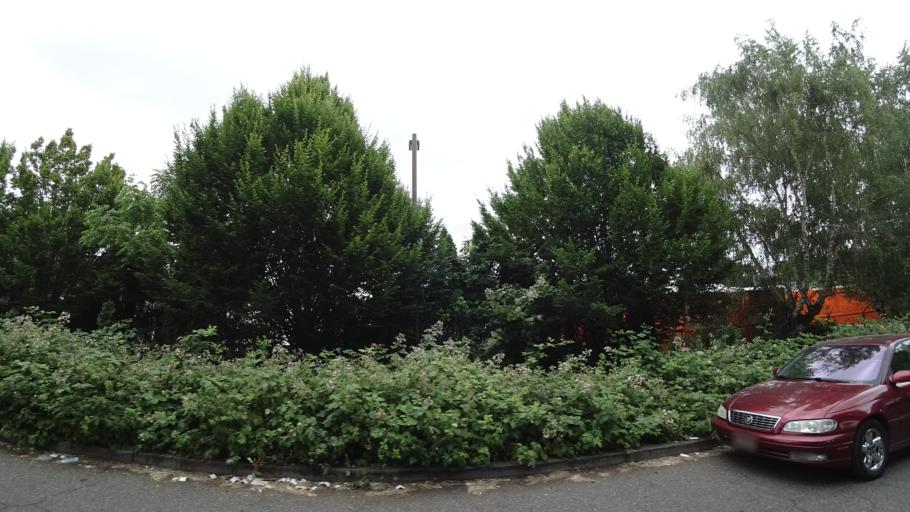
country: US
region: Washington
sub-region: Clark County
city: Vancouver
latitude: 45.5807
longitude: -122.6621
